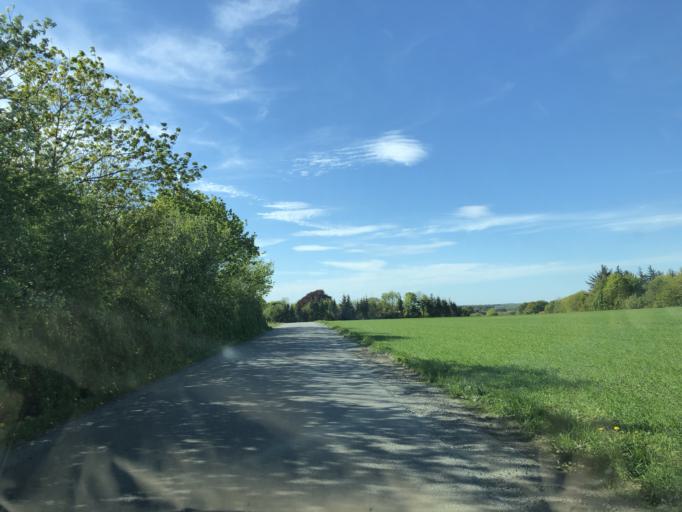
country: DK
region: Central Jutland
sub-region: Ringkobing-Skjern Kommune
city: Videbaek
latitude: 56.1694
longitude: 8.5318
